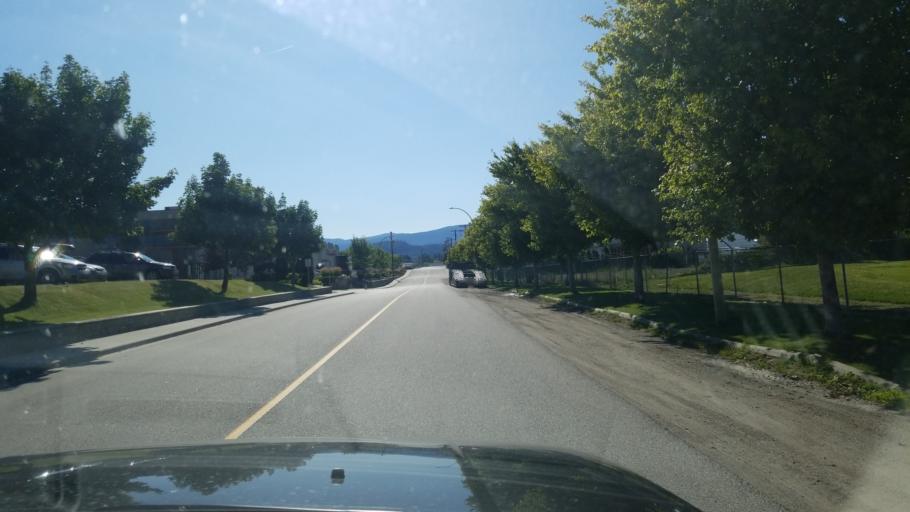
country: CA
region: British Columbia
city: Kelowna
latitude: 49.9220
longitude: -119.3799
